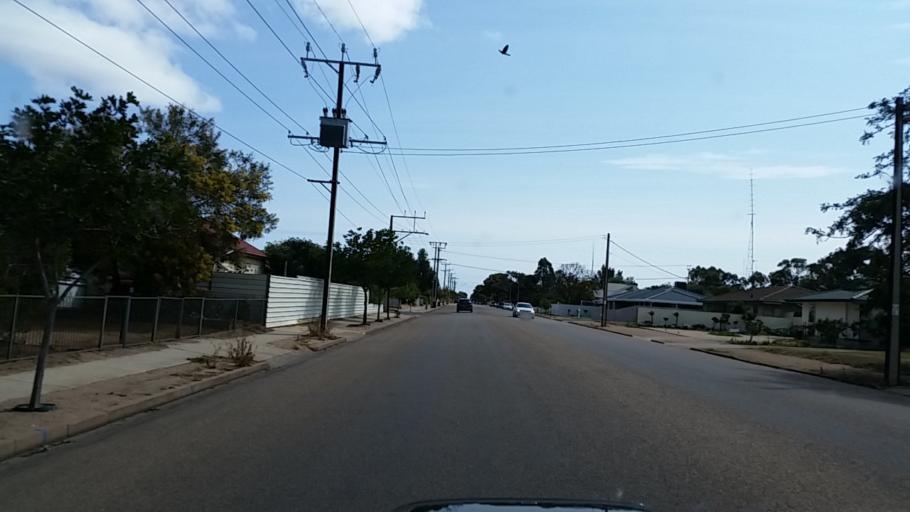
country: AU
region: South Australia
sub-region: Port Pirie City and Dists
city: Port Pirie
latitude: -33.1894
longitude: 138.0011
